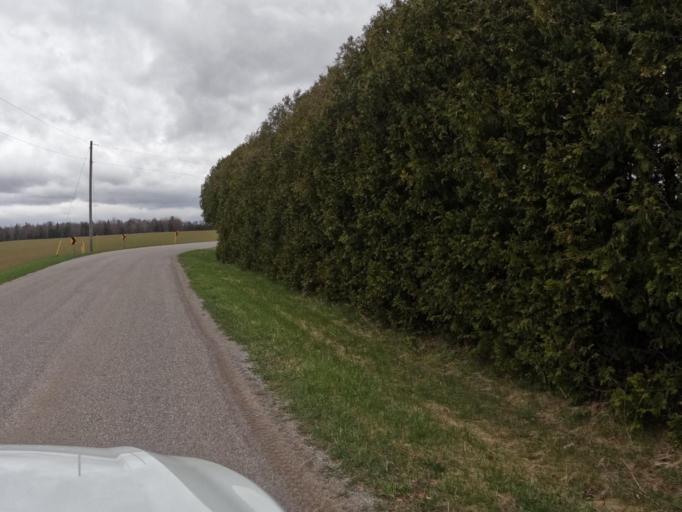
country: CA
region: Ontario
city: Norfolk County
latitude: 42.9678
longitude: -80.4296
